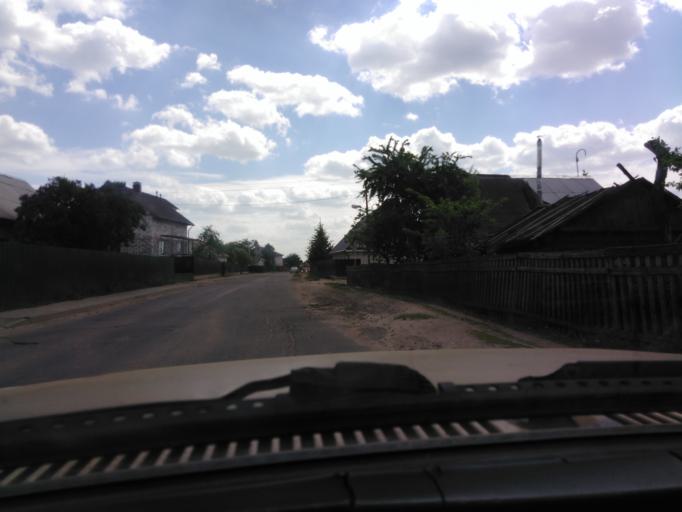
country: BY
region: Mogilev
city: Mahilyow
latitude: 53.9364
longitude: 30.3213
